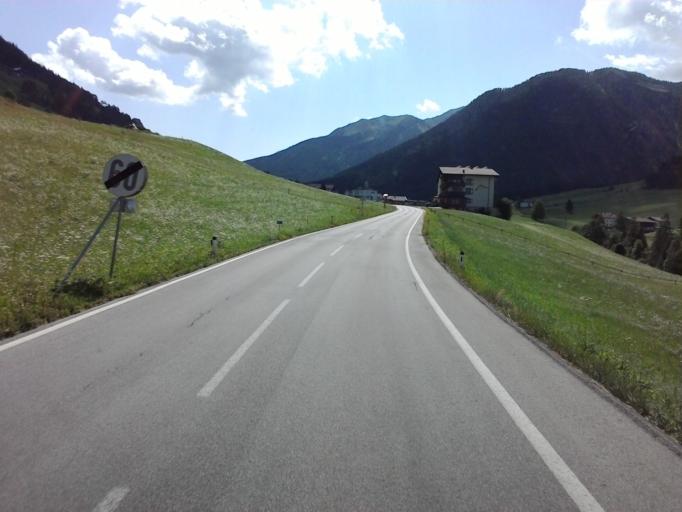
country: AT
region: Tyrol
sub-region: Politischer Bezirk Lienz
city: Kartitsch
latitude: 46.7297
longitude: 12.4904
